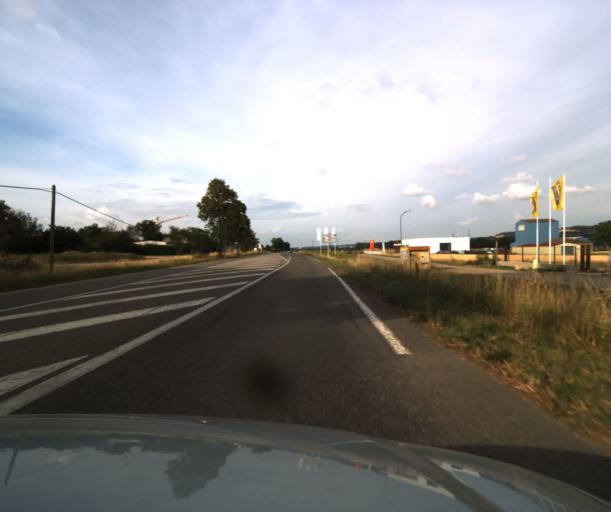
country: FR
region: Midi-Pyrenees
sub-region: Departement du Tarn-et-Garonne
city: Beaumont-de-Lomagne
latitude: 43.9013
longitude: 1.0321
